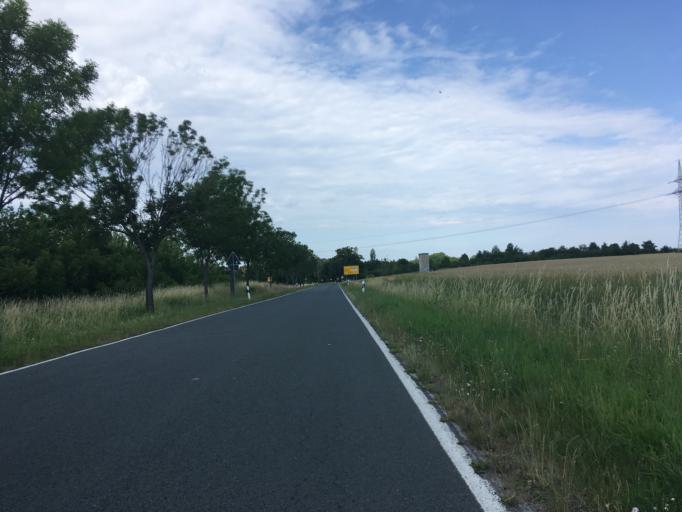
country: DE
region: Saxony-Anhalt
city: Baalberge
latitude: 51.7791
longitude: 11.7804
